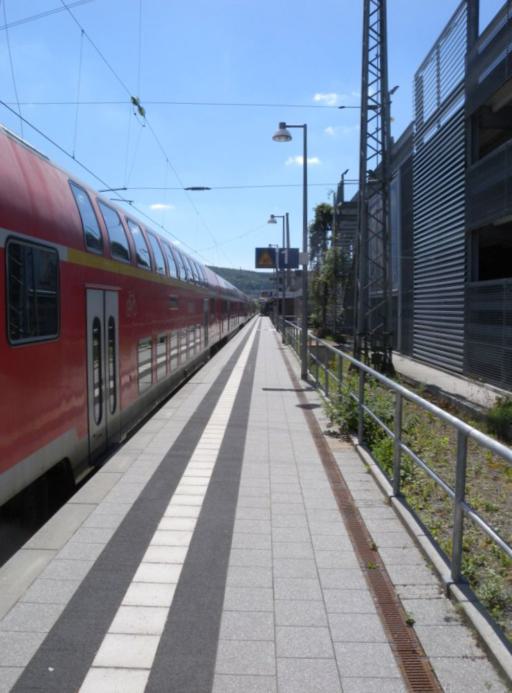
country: DE
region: Baden-Wuerttemberg
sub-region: Karlsruhe Region
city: Obrigheim
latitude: 49.3495
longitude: 9.1121
